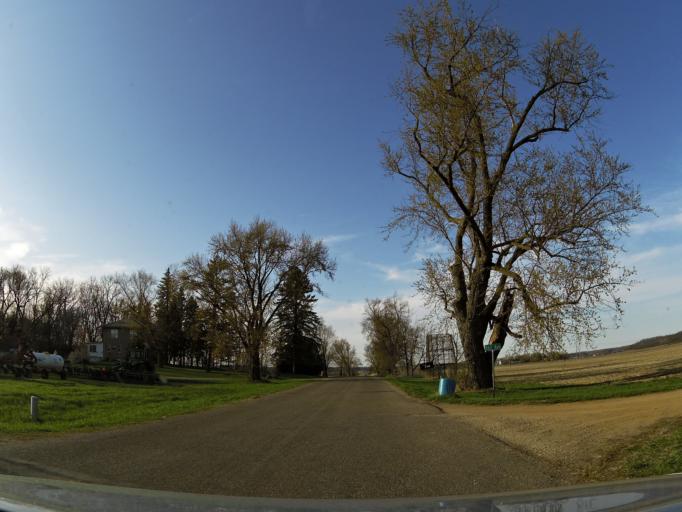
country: US
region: Minnesota
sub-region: Washington County
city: Afton
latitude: 44.8519
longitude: -92.7159
